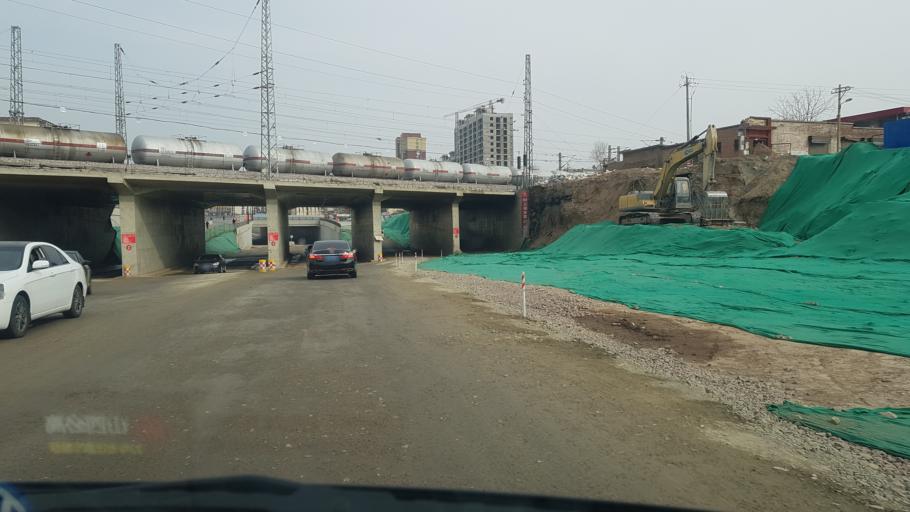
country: CN
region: Shanxi Sheng
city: Yuci
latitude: 37.6902
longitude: 112.7300
